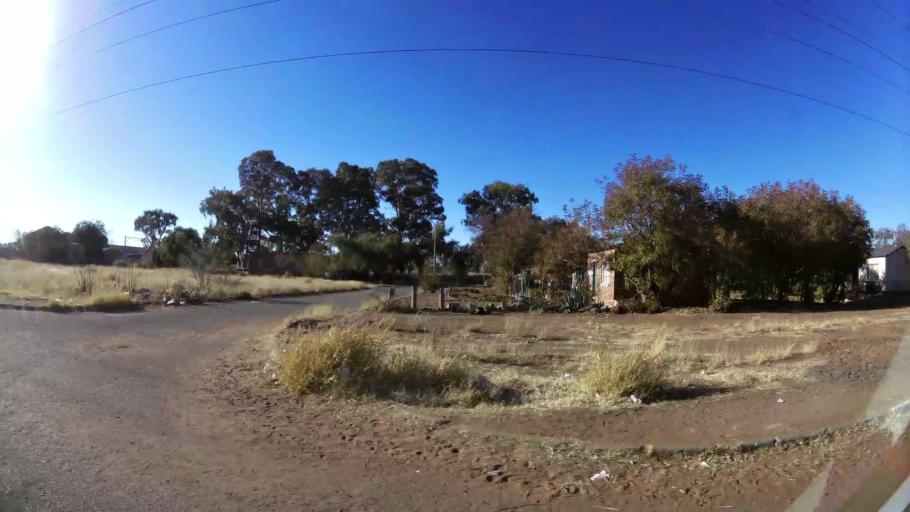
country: ZA
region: Northern Cape
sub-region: Frances Baard District Municipality
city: Kimberley
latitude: -28.7605
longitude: 24.7837
